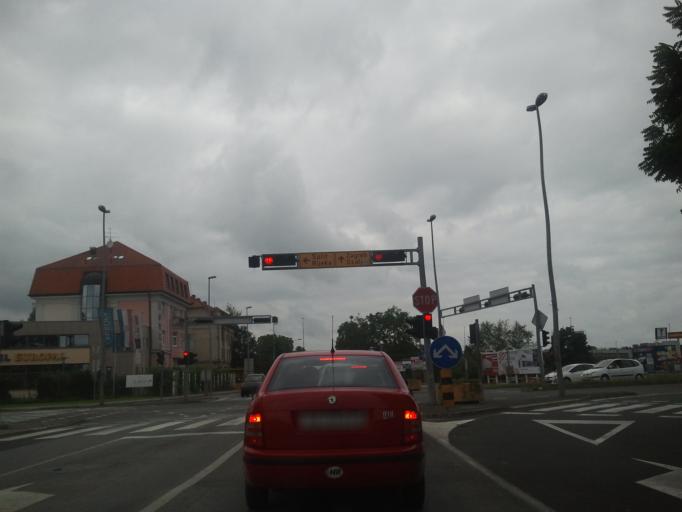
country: HR
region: Karlovacka
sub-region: Grad Karlovac
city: Karlovac
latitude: 45.5113
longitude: 15.5473
